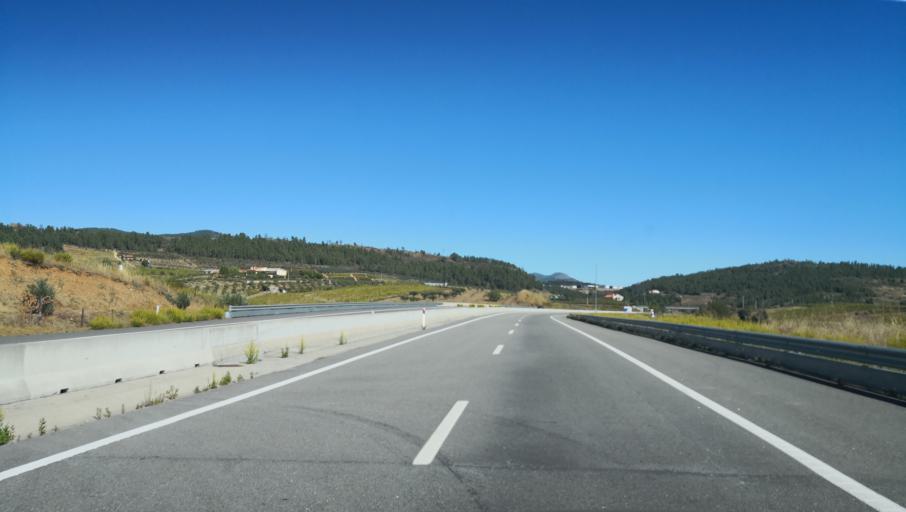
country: PT
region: Vila Real
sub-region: Murca
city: Murca
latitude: 41.4036
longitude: -7.4338
